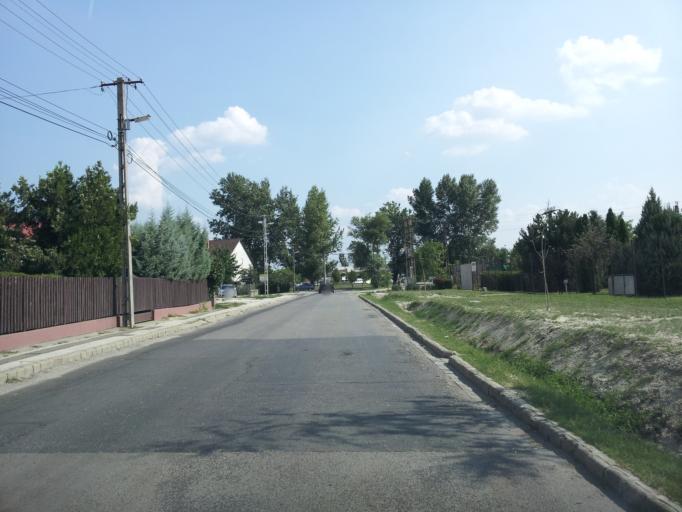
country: HU
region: Pest
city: Szigetszentmiklos
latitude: 47.3392
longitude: 19.0295
